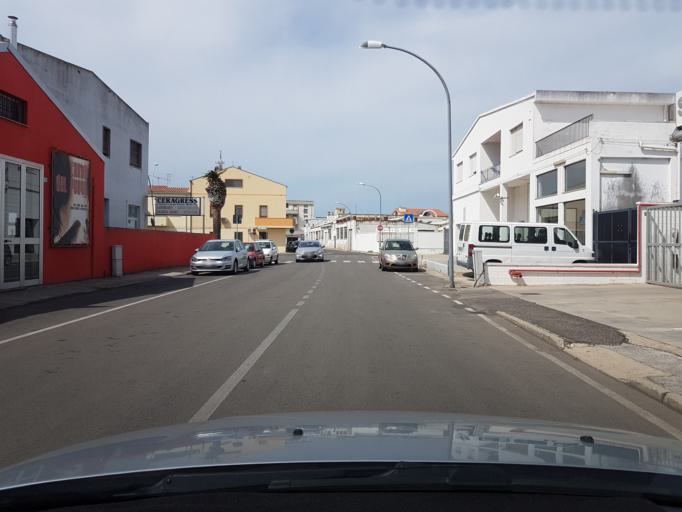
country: IT
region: Sardinia
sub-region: Provincia di Oristano
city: Oristano
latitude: 39.9115
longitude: 8.5899
